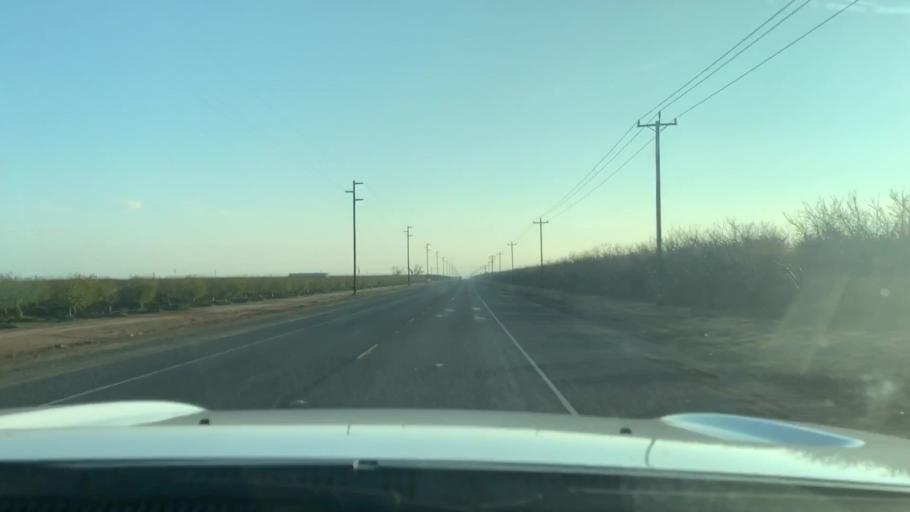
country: US
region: California
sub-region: Kern County
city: Wasco
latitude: 35.6011
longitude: -119.4795
